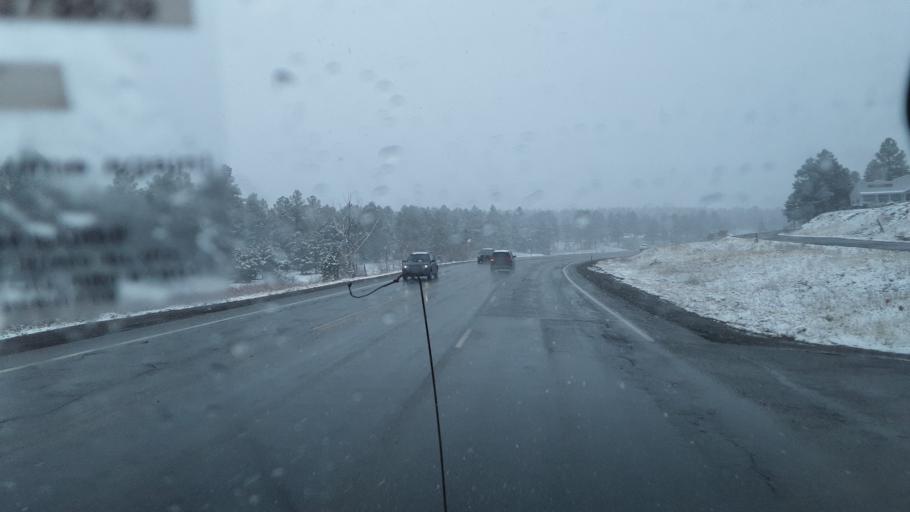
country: US
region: Colorado
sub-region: Archuleta County
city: Pagosa Springs
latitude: 37.2670
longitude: -107.0242
